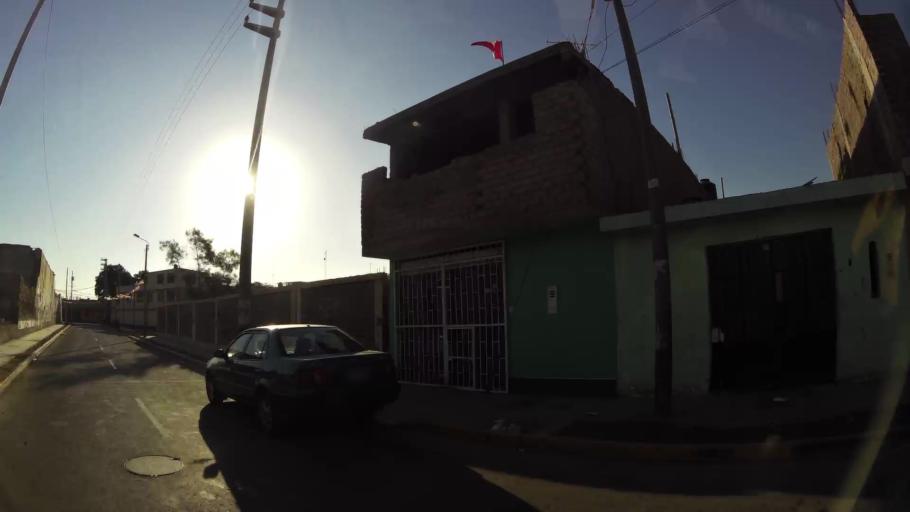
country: PE
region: Ica
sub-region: Provincia de Ica
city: Ica
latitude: -14.0671
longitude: -75.7210
